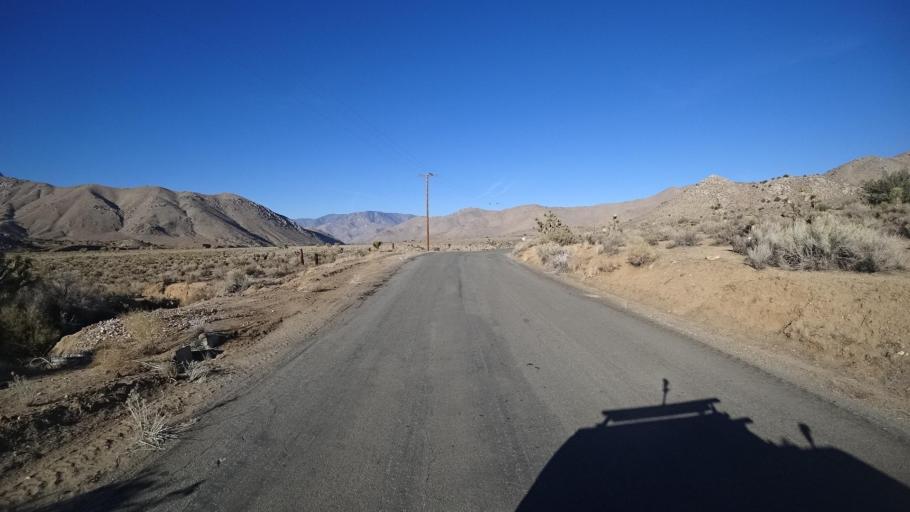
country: US
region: California
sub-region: Kern County
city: Weldon
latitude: 35.5862
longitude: -118.2437
